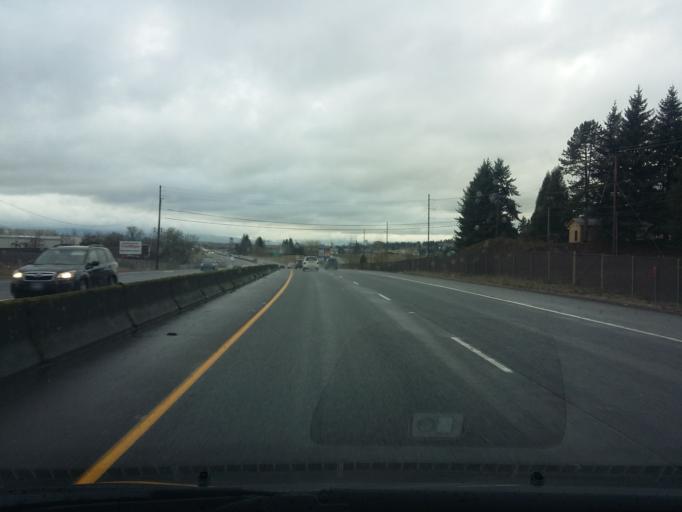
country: US
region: Washington
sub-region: Clark County
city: Vancouver
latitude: 45.6184
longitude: -122.6246
